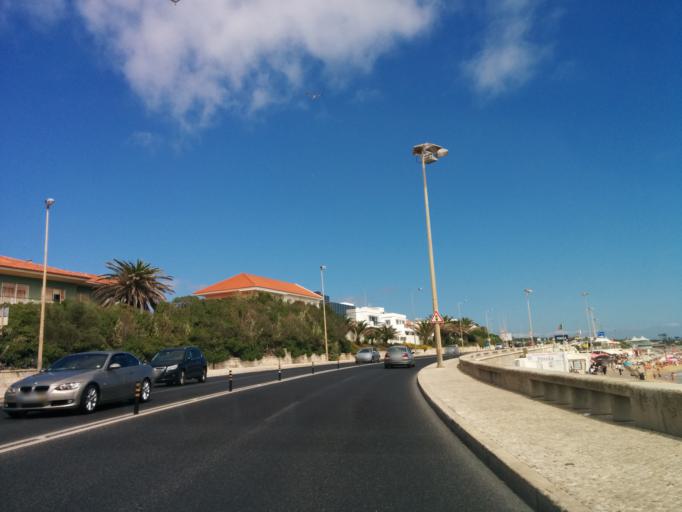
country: PT
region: Lisbon
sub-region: Cascais
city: Parede
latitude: 38.6819
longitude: -9.3424
